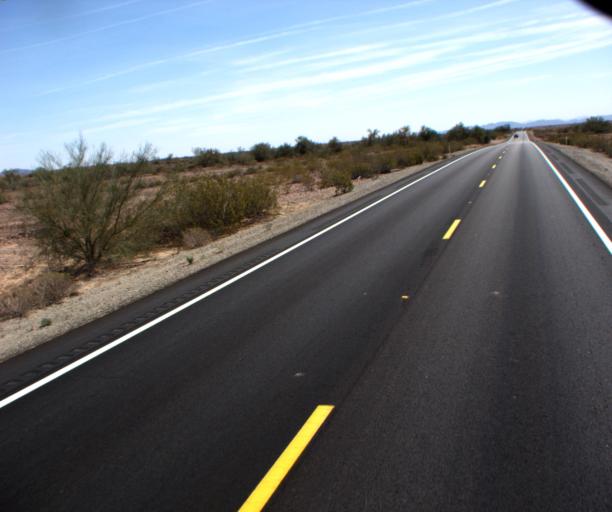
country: US
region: Arizona
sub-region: Yuma County
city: Wellton
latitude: 33.0710
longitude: -114.2943
